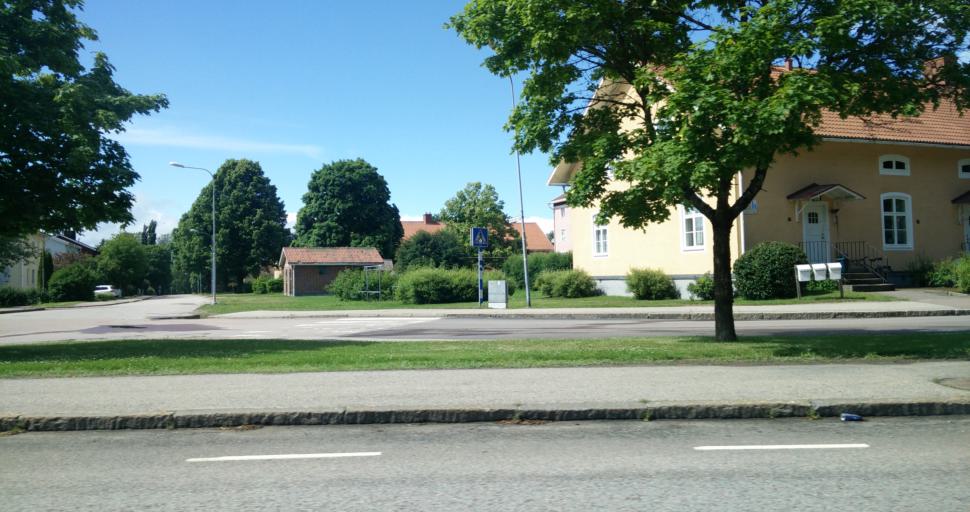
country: SE
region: Vaermland
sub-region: Hagfors Kommun
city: Hagfors
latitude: 60.0327
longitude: 13.7042
